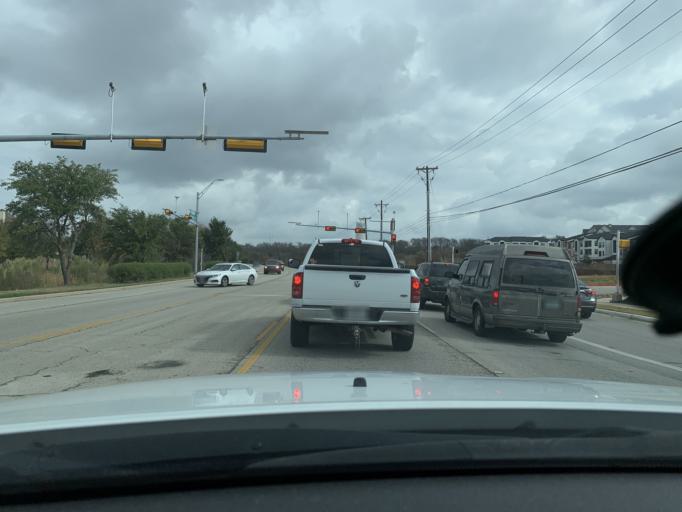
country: US
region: Texas
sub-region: Williamson County
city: Round Rock
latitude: 30.5626
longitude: -97.6768
